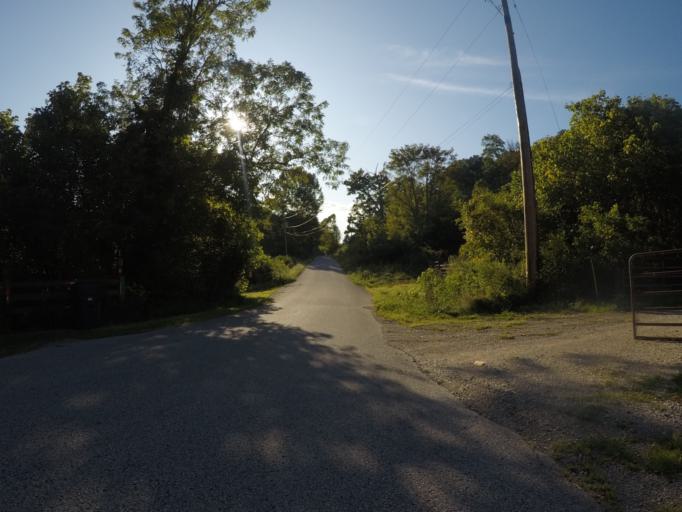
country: US
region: Ohio
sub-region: Lawrence County
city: Burlington
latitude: 38.5237
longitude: -82.5093
